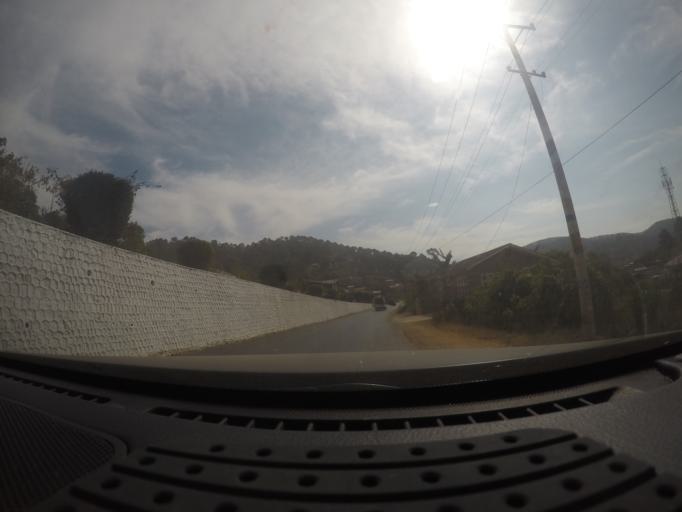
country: MM
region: Mandalay
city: Yamethin
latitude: 20.6357
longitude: 96.5729
